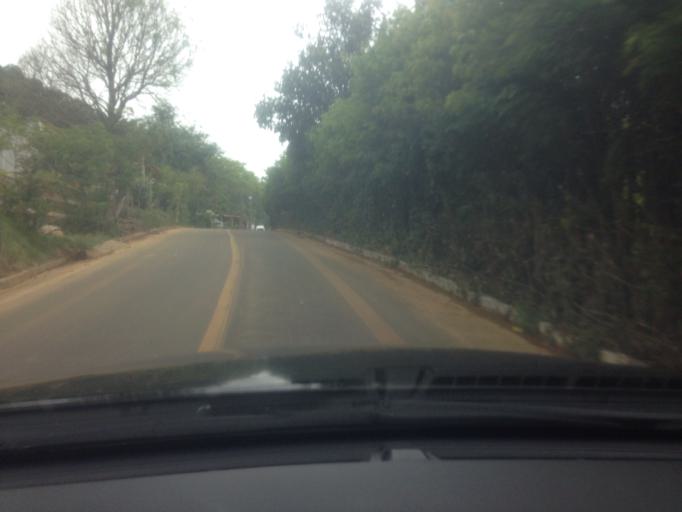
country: BR
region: Espirito Santo
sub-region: Guarapari
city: Guarapari
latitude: -20.5581
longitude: -40.5537
